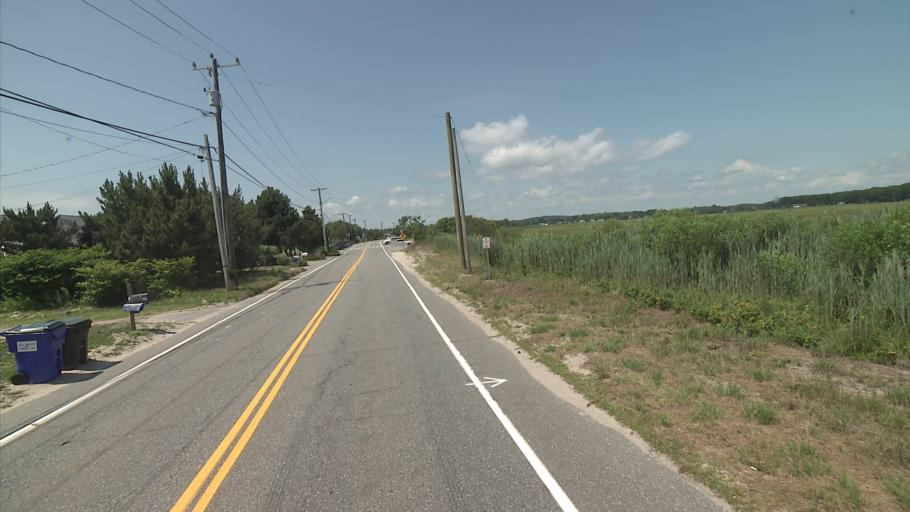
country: US
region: Connecticut
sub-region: Middlesex County
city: Saybrook Manor
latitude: 41.2683
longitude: -72.3918
